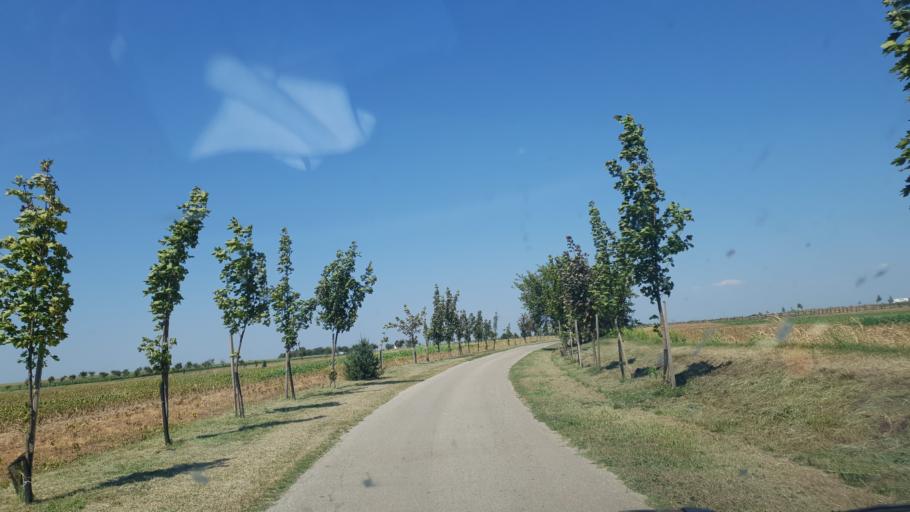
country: RS
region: Autonomna Pokrajina Vojvodina
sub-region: Juznobacki Okrug
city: Kovilj
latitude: 45.2079
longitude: 20.0629
